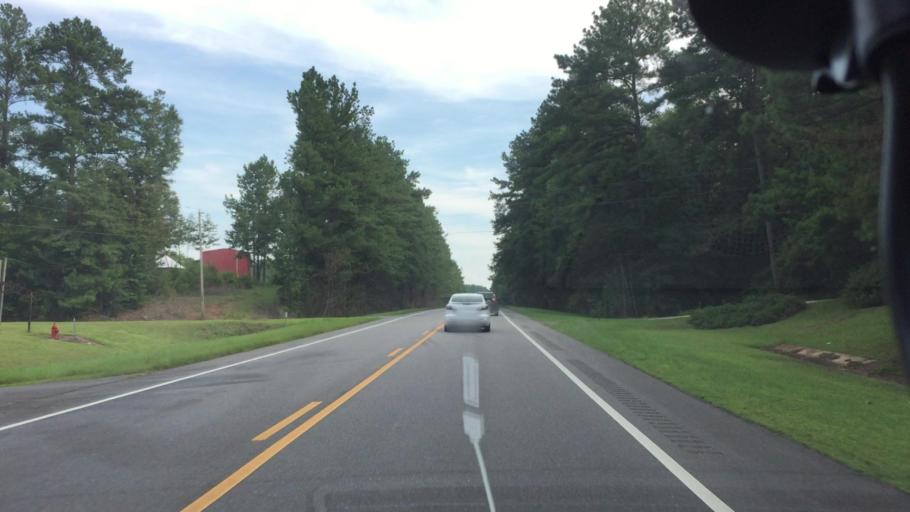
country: US
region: Alabama
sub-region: Coffee County
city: New Brockton
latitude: 31.5611
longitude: -85.9240
